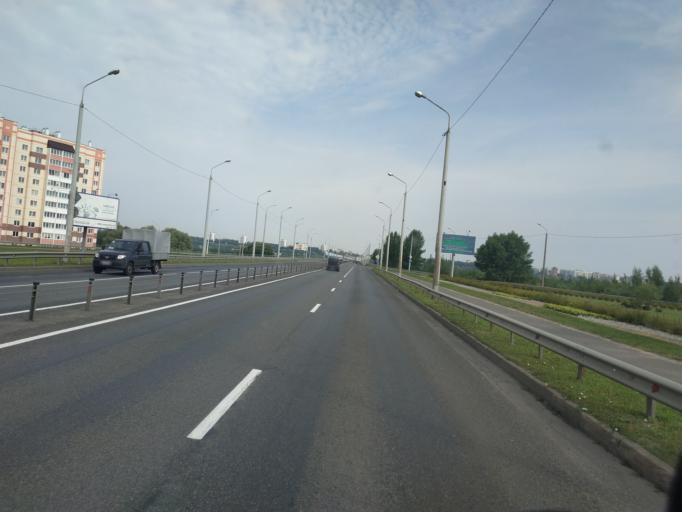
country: BY
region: Mogilev
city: Mahilyow
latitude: 53.8838
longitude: 30.3803
